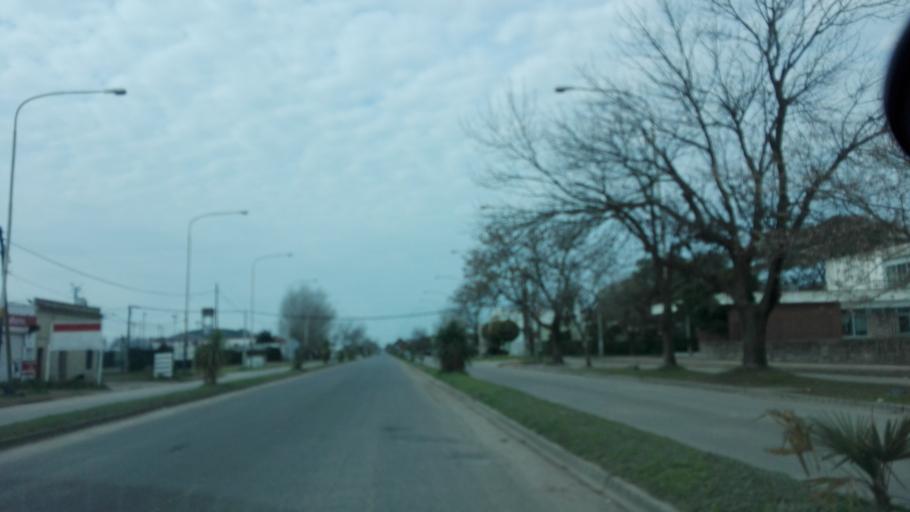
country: AR
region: Buenos Aires
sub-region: Partido de Chascomus
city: Chascomus
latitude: -35.5767
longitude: -58.0055
